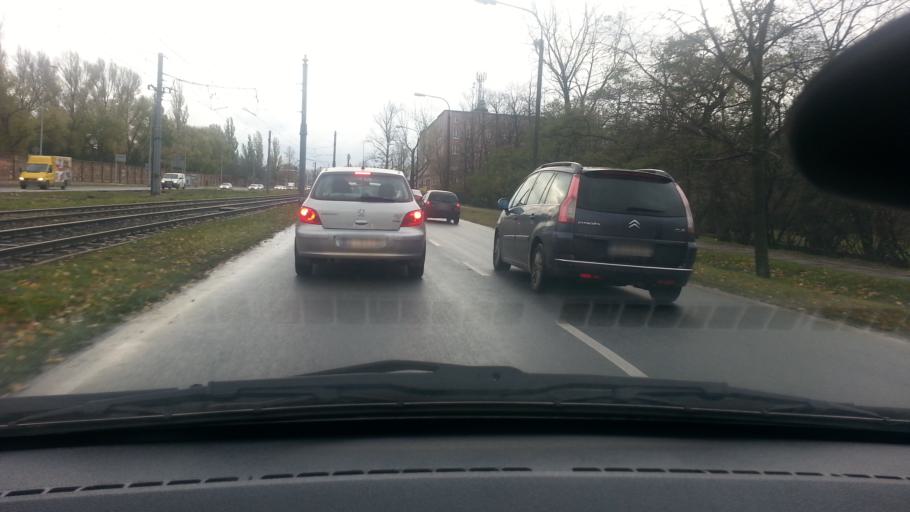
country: PL
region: Masovian Voivodeship
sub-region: Warszawa
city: Targowek
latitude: 52.2801
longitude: 21.0262
